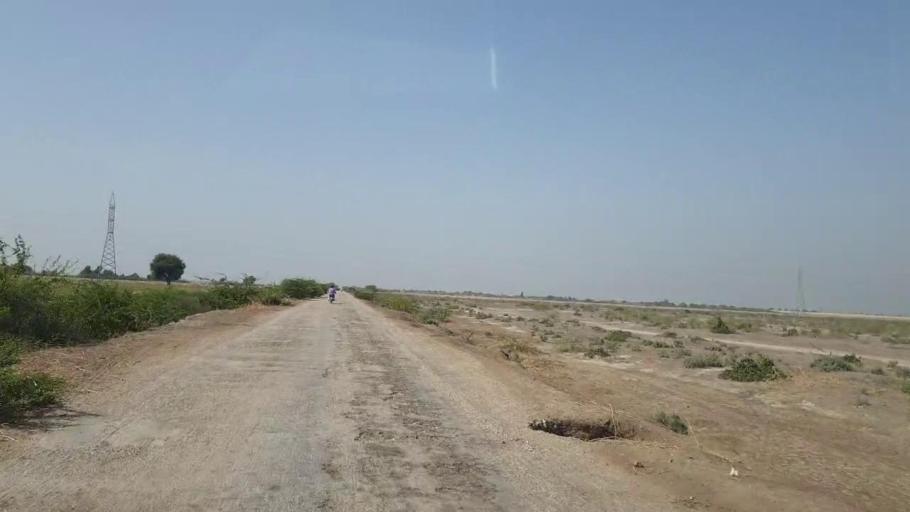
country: PK
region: Sindh
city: Naukot
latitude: 25.0146
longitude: 69.4594
